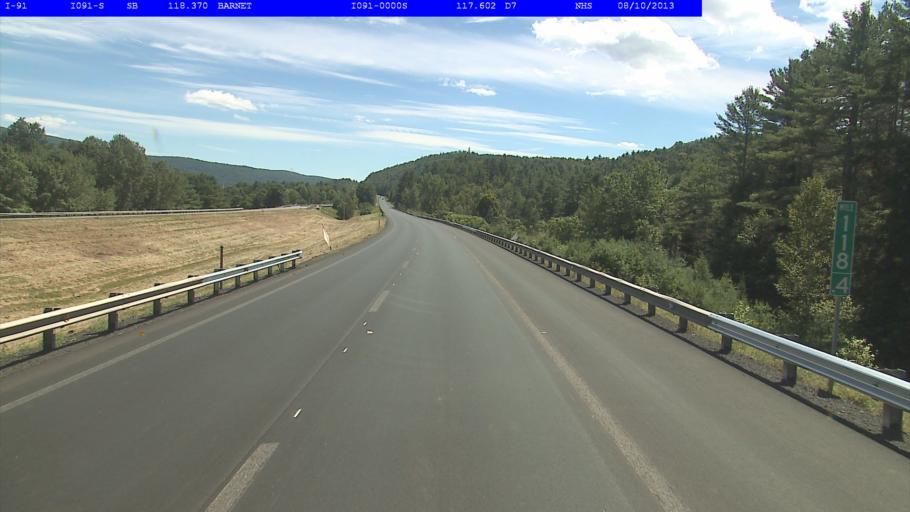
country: US
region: New Hampshire
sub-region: Grafton County
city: Woodsville
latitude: 44.2710
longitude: -72.0724
